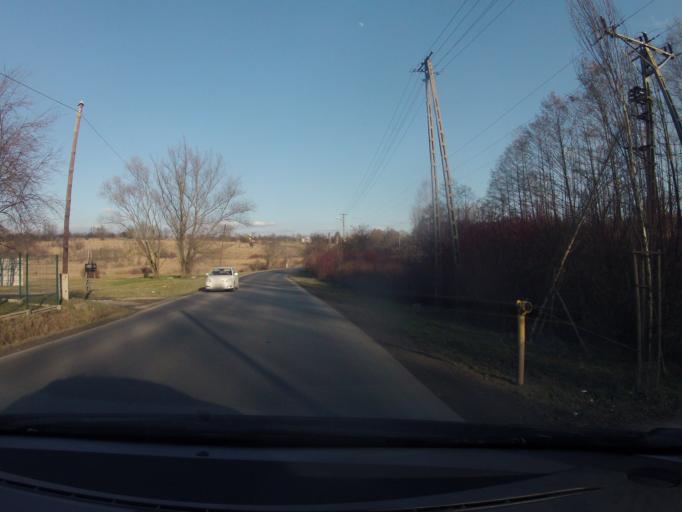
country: PL
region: Lesser Poland Voivodeship
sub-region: Powiat krakowski
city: Ochojno
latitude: 49.9864
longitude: 20.0117
